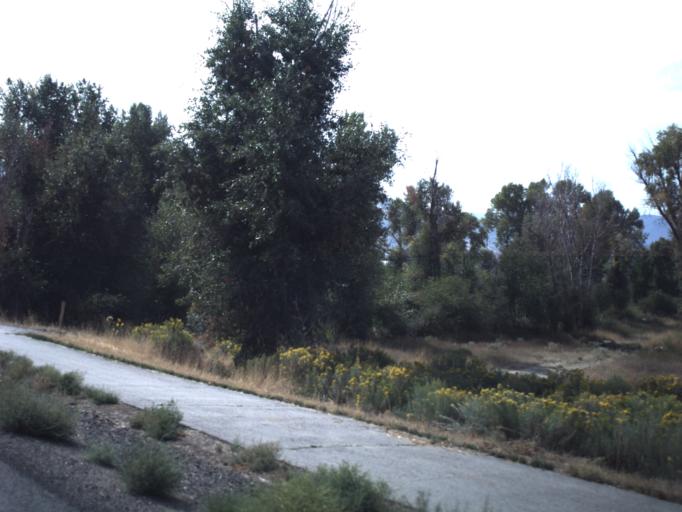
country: US
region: Utah
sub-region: Wasatch County
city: Midway
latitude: 40.5081
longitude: -111.4512
